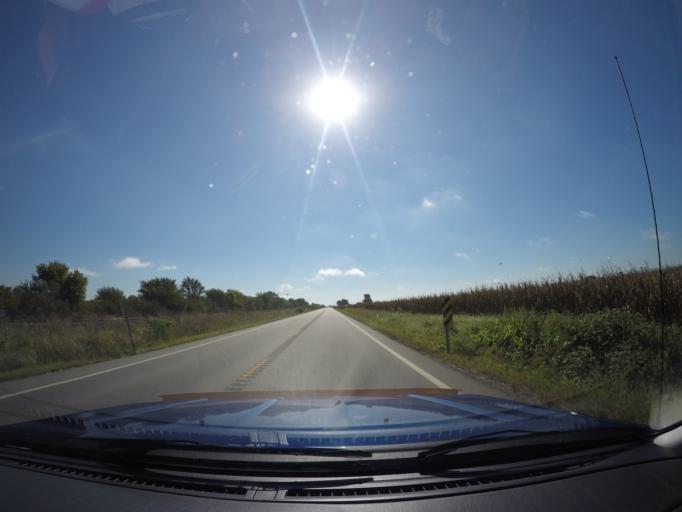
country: US
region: Kansas
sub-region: Shawnee County
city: Rossville
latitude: 39.1290
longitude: -95.9387
